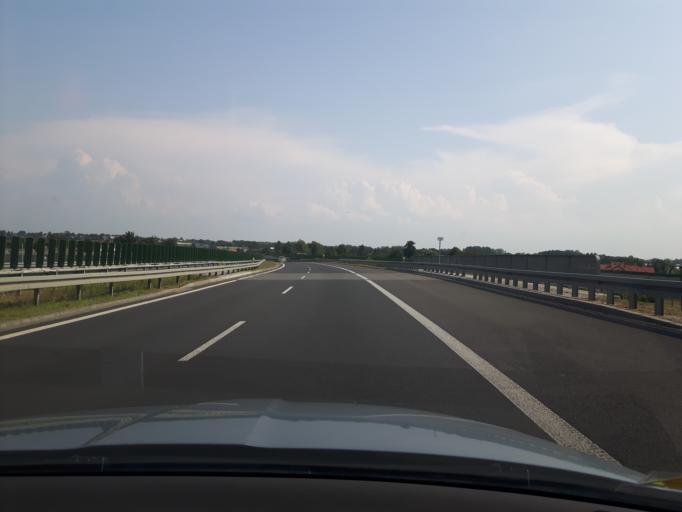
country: PL
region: Masovian Voivodeship
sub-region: Powiat plonski
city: Plonsk
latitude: 52.6131
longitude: 20.3891
